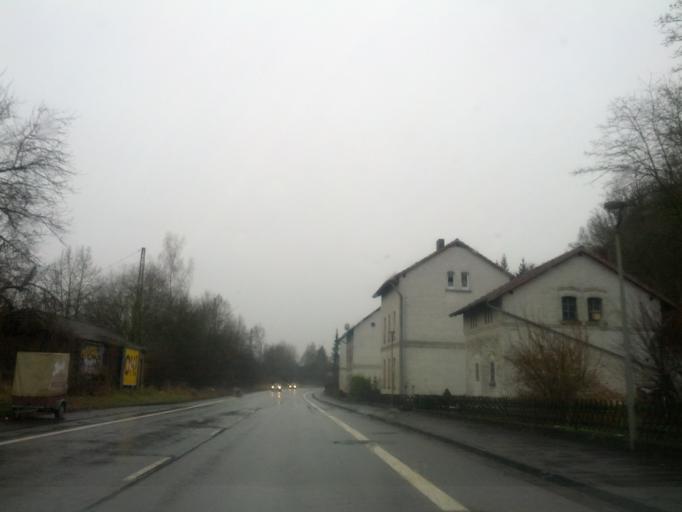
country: DE
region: Hesse
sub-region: Regierungsbezirk Kassel
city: Eschwege
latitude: 51.1917
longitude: 9.9946
